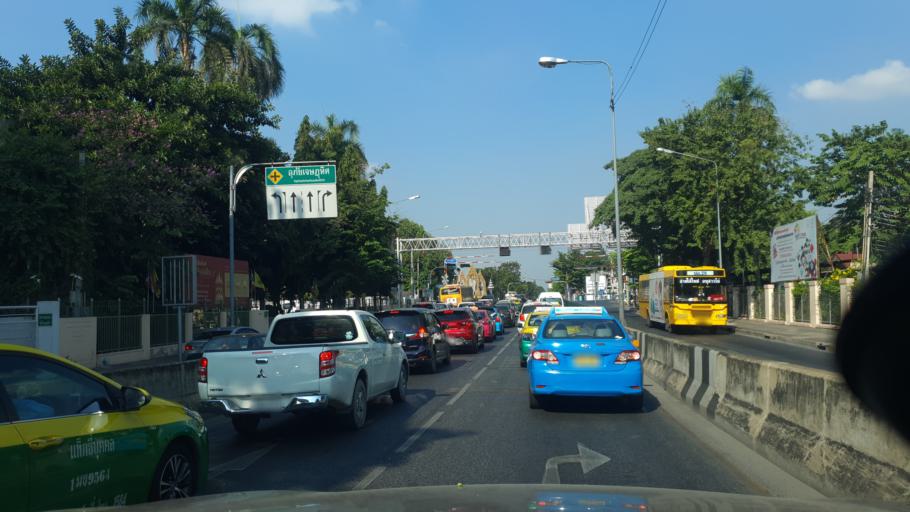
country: TH
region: Bangkok
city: Dusit
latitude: 13.7700
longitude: 100.5271
